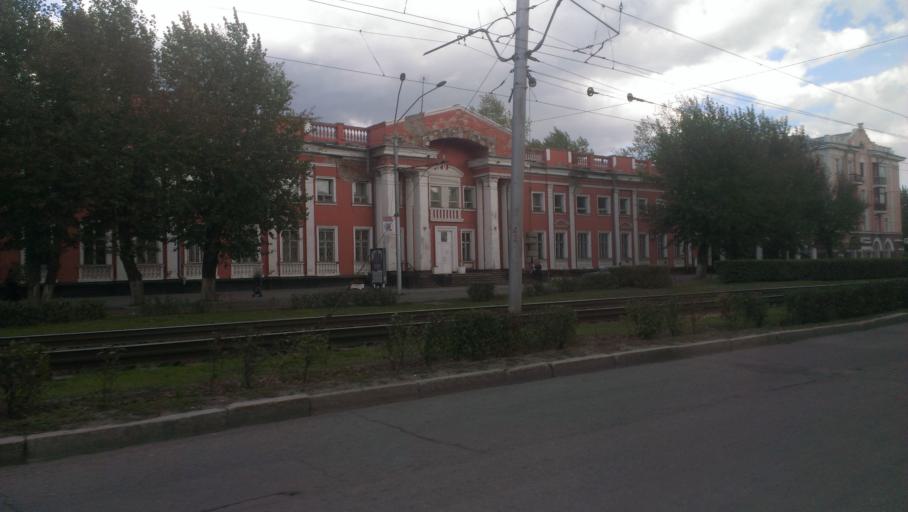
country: RU
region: Altai Krai
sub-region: Gorod Barnaulskiy
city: Barnaul
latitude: 53.3587
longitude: 83.7653
